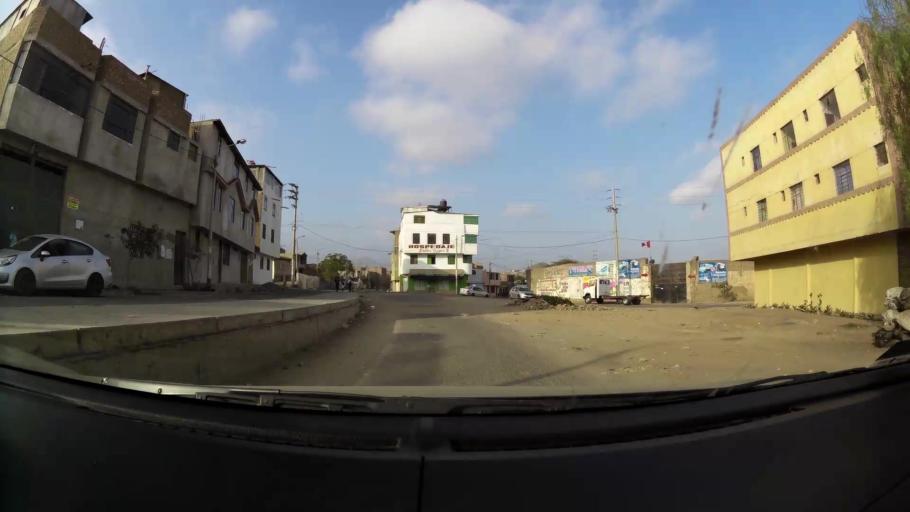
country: PE
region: La Libertad
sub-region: Provincia de Trujillo
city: El Porvenir
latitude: -8.0874
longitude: -79.0179
